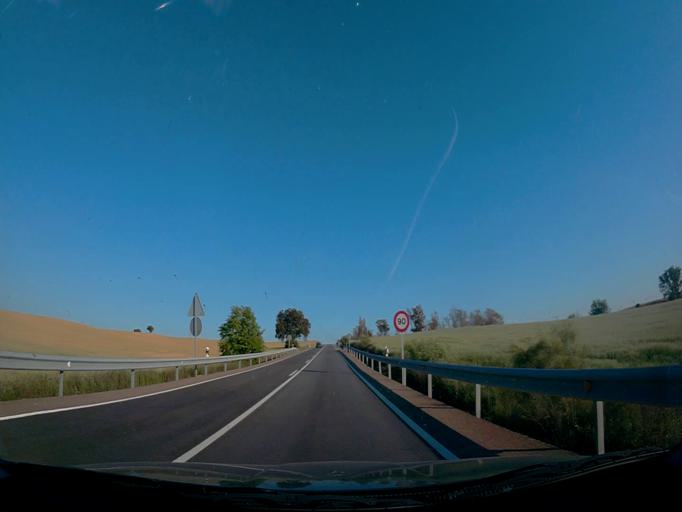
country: ES
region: Castille-La Mancha
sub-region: Province of Toledo
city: Hormigos
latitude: 40.1200
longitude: -4.4076
